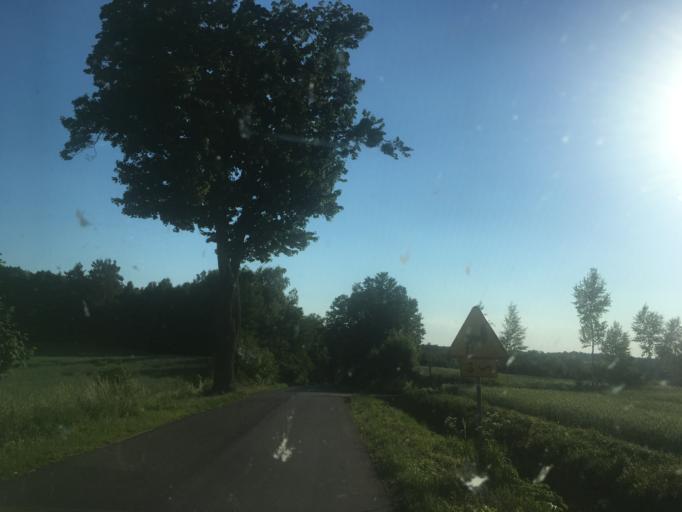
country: PL
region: Warmian-Masurian Voivodeship
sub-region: Powiat ostrodzki
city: Gierzwald
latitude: 53.6266
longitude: 20.0479
